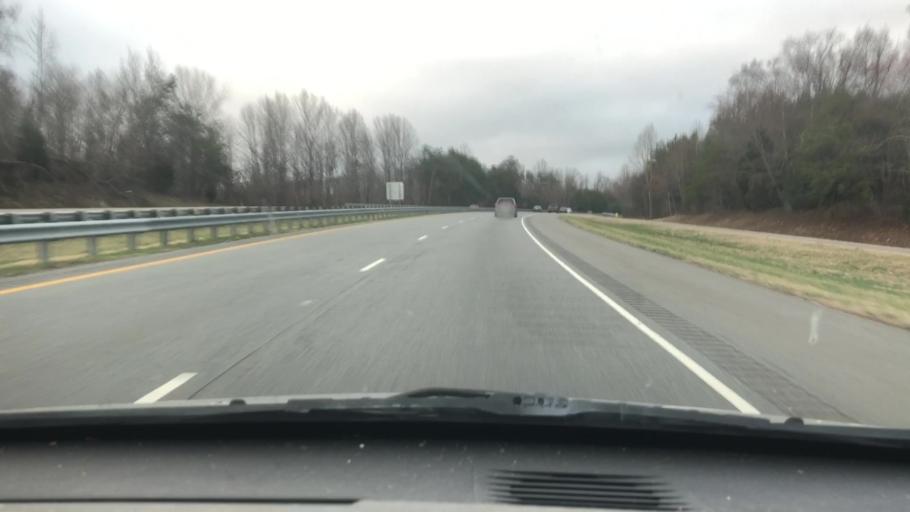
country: US
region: North Carolina
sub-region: Rockingham County
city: Stoneville
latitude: 36.4490
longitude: -79.9308
